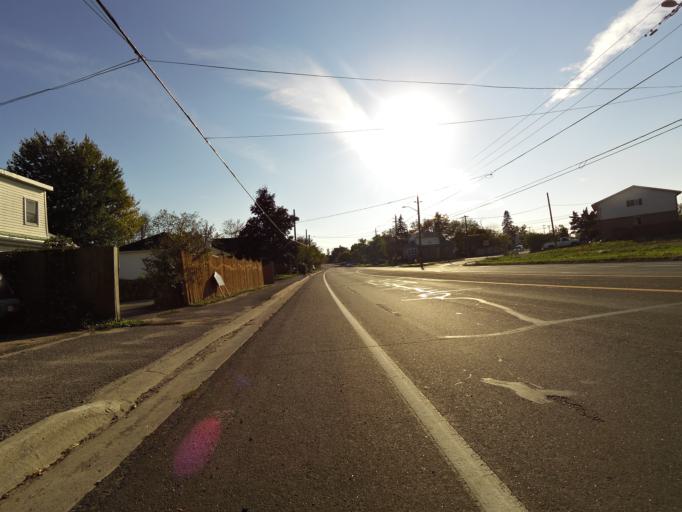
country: CA
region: Ontario
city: Kingston
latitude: 44.2630
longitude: -76.4792
